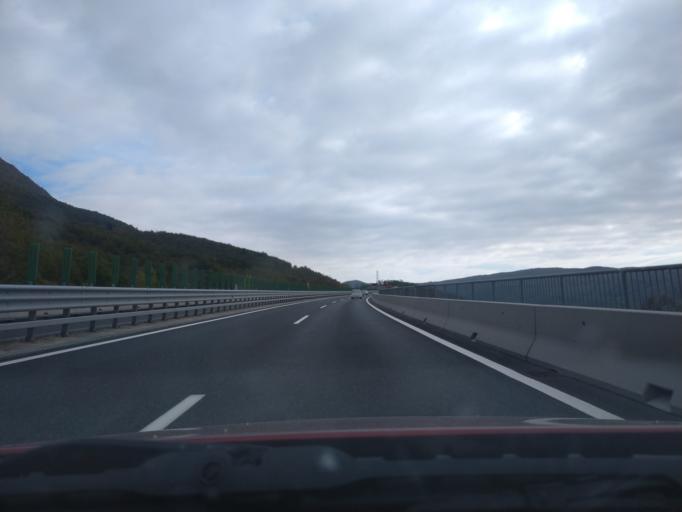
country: SI
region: Vipava
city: Vipava
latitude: 45.7774
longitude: 14.0198
